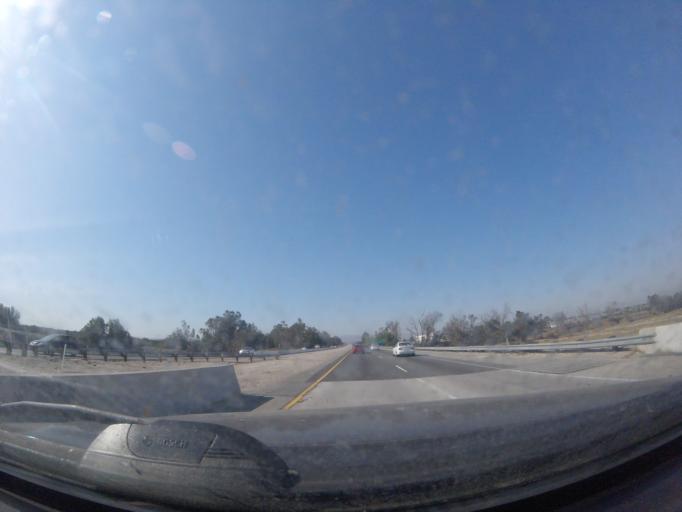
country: US
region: California
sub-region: San Bernardino County
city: Highland
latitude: 34.0927
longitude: -117.2007
